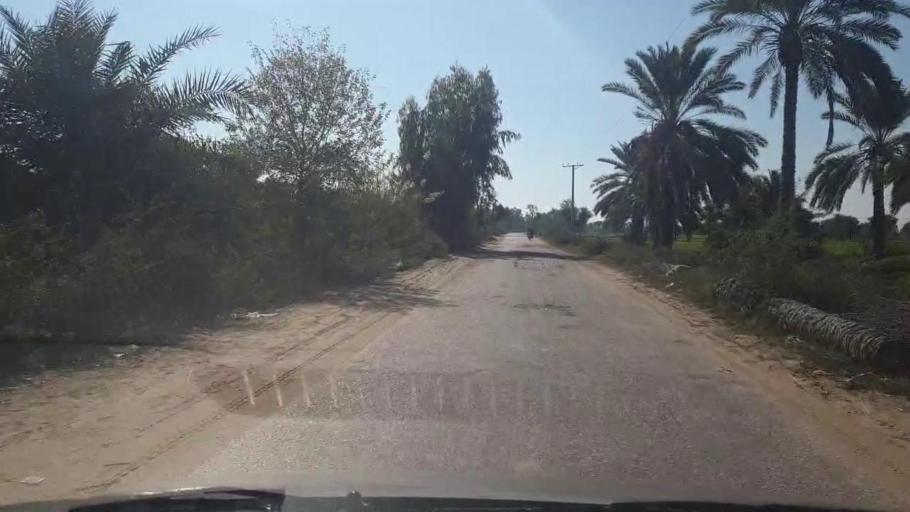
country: PK
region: Sindh
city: Bozdar
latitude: 27.0908
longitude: 68.6244
